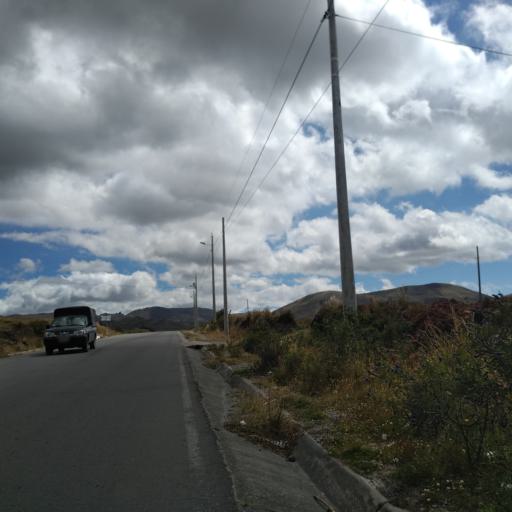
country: EC
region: Cotopaxi
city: Saquisili
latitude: -0.7527
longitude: -78.7321
